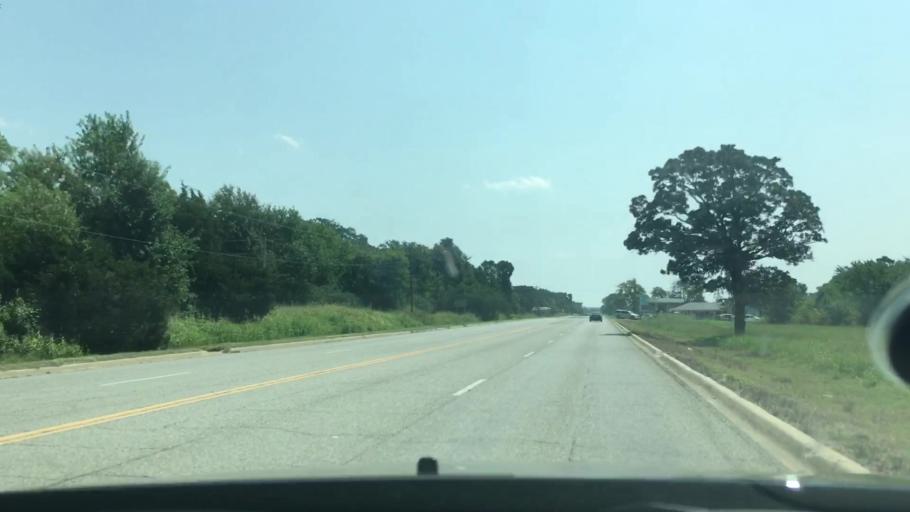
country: US
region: Oklahoma
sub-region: Atoka County
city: Atoka
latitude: 34.3033
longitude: -95.9995
